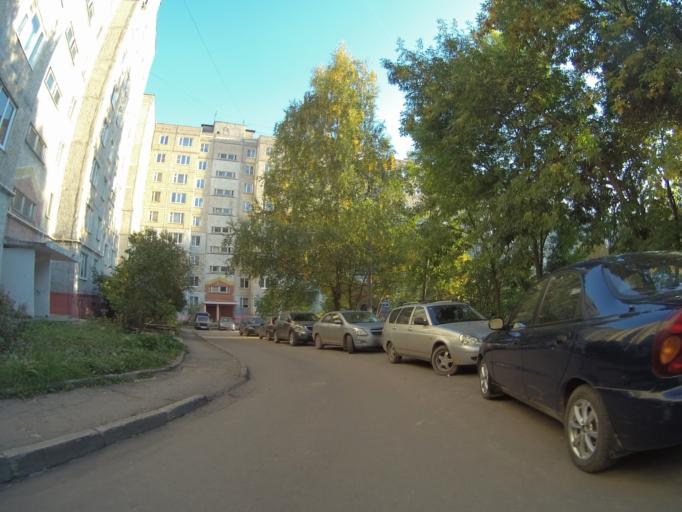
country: RU
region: Vladimir
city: Vladimir
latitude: 56.1079
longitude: 40.3548
